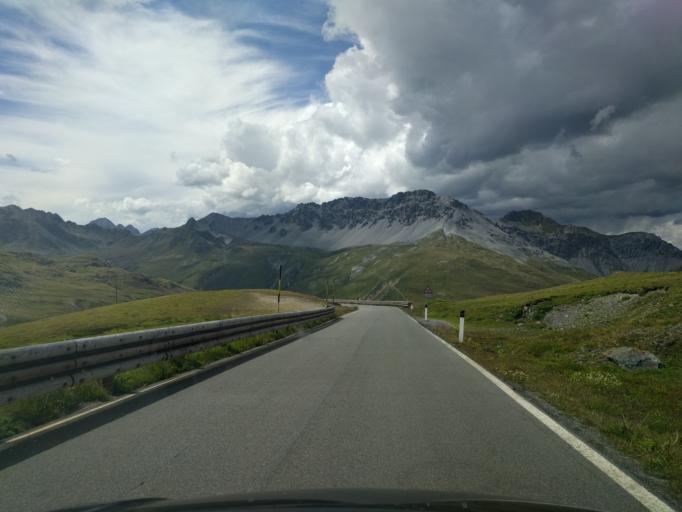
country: IT
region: Lombardy
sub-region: Provincia di Sondrio
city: Sant'Antonio
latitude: 46.5327
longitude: 10.4463
